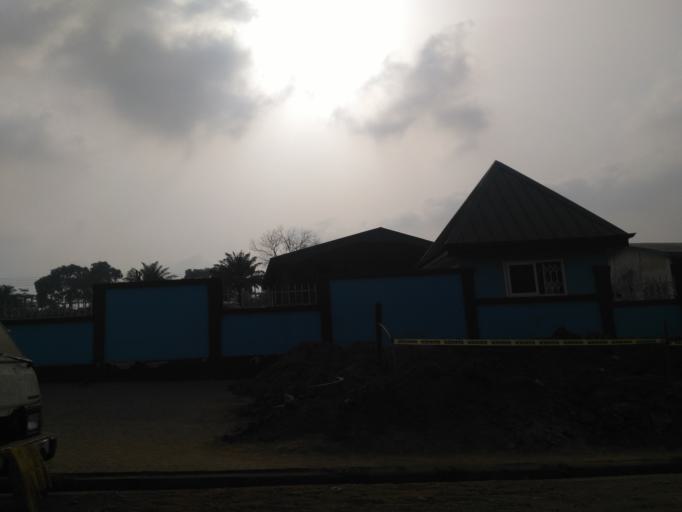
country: GH
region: Ashanti
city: Kumasi
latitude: 6.6930
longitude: -1.5944
